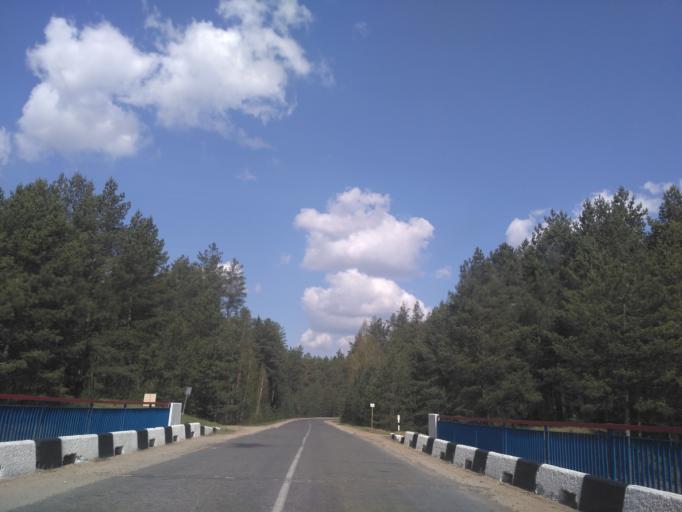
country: BY
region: Minsk
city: Radashkovichy
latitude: 54.1705
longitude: 27.2449
